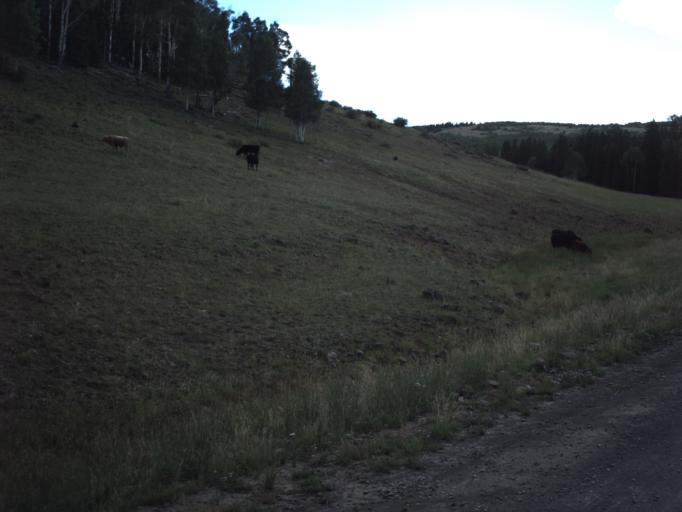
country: US
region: Utah
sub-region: Piute County
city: Junction
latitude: 38.2370
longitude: -112.3652
